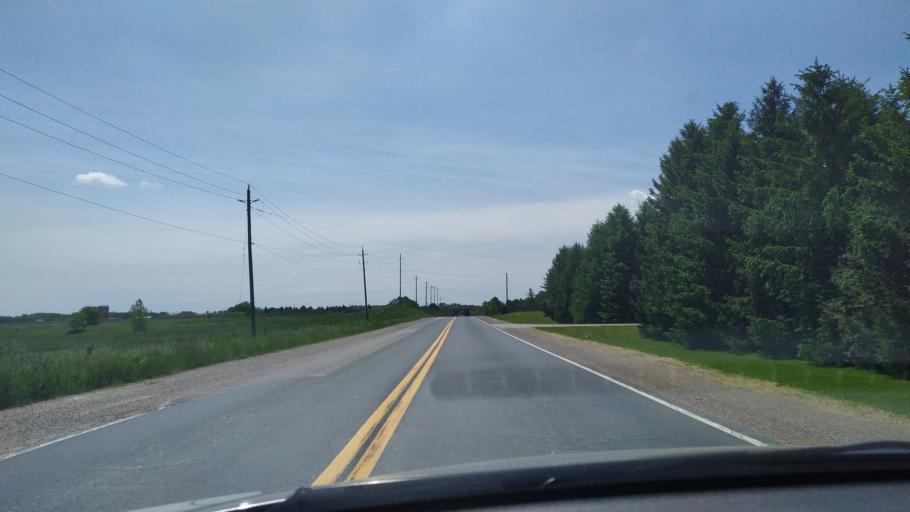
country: CA
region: Ontario
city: Ingersoll
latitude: 43.0097
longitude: -80.9627
